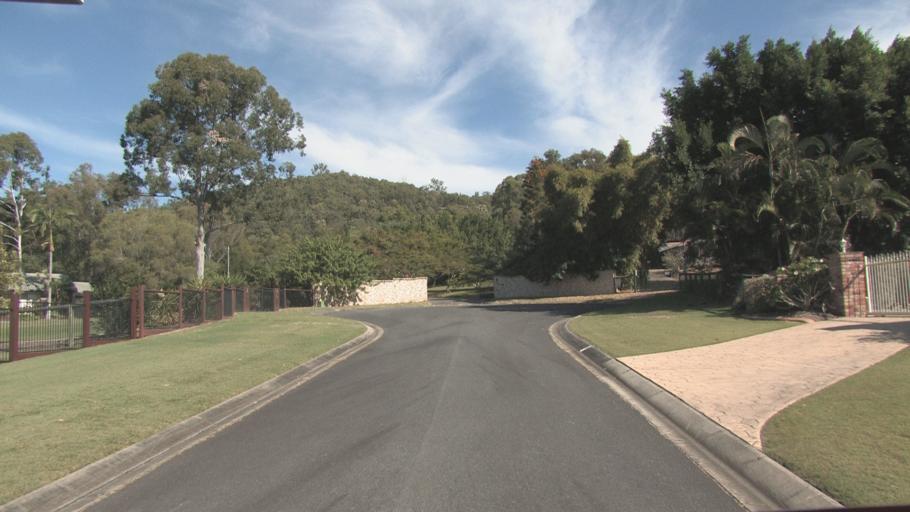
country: AU
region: Queensland
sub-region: Logan
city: Windaroo
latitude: -27.7607
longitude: 153.1819
